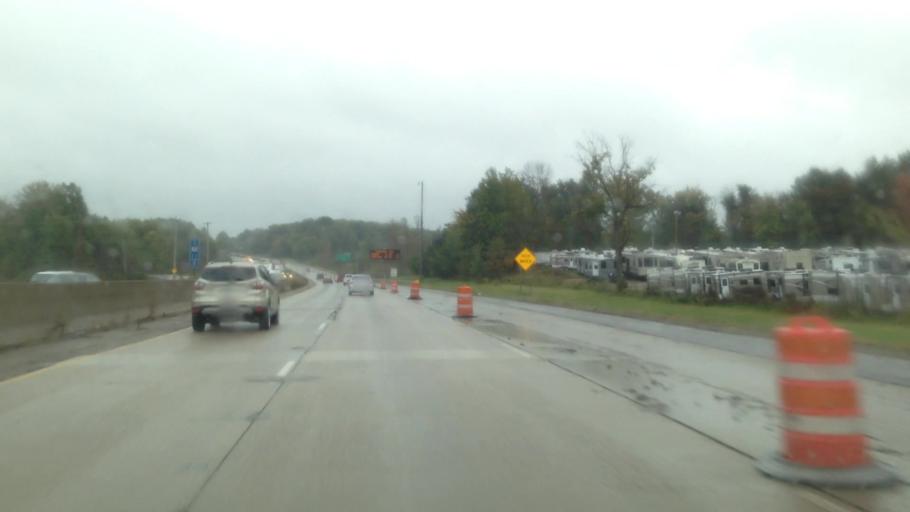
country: US
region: Ohio
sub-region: Summit County
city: Boston Heights
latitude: 41.2190
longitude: -81.4893
